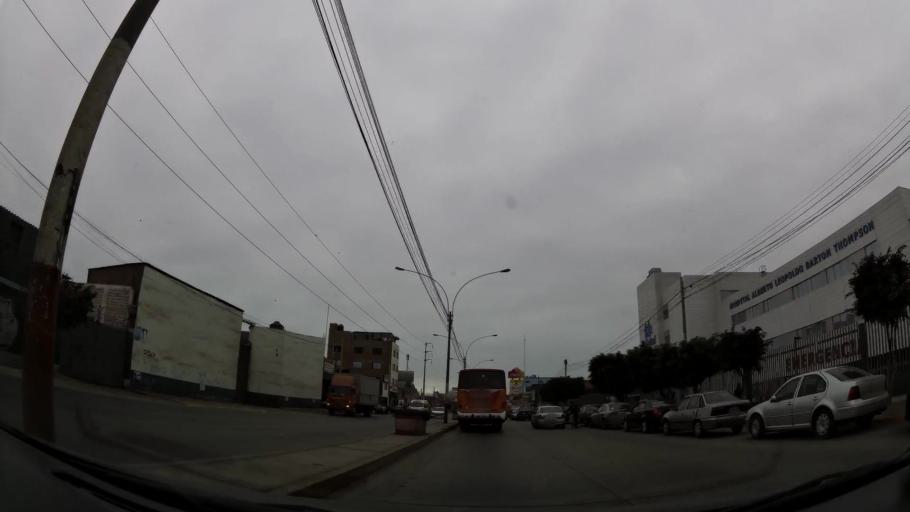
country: PE
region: Callao
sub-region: Callao
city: Callao
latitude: -12.0492
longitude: -77.1073
